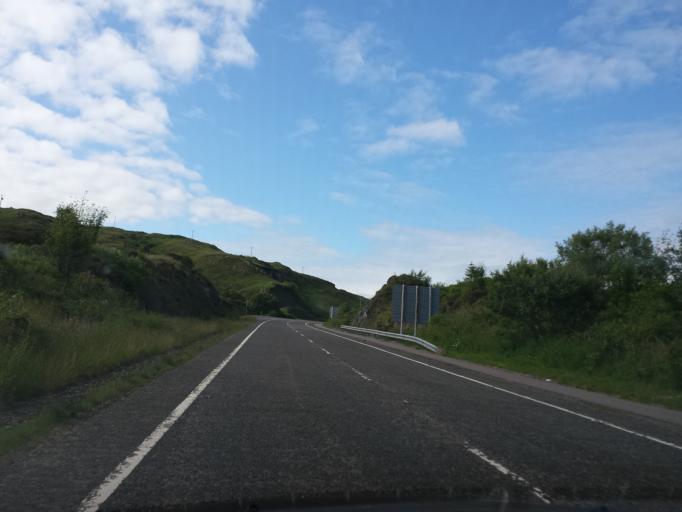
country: GB
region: Scotland
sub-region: Argyll and Bute
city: Isle Of Mull
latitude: 56.9765
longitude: -5.8281
